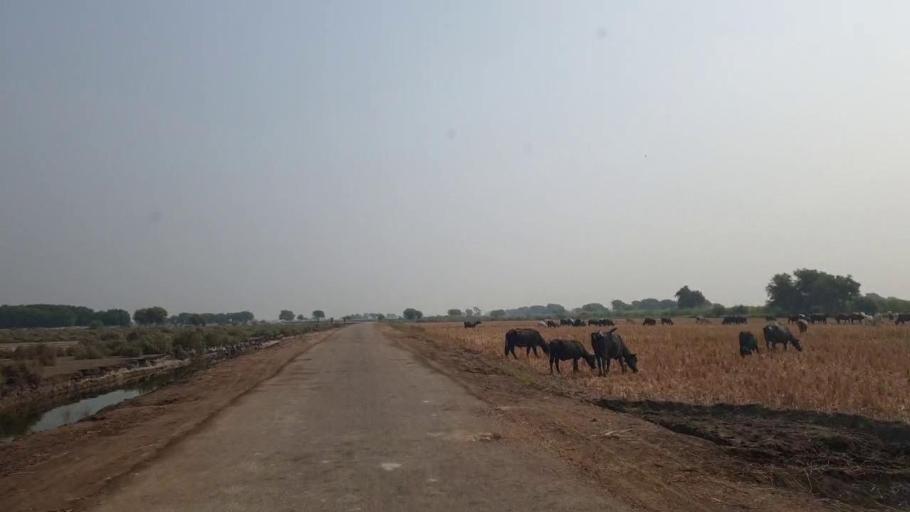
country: PK
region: Sindh
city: Matli
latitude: 25.1303
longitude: 68.6964
